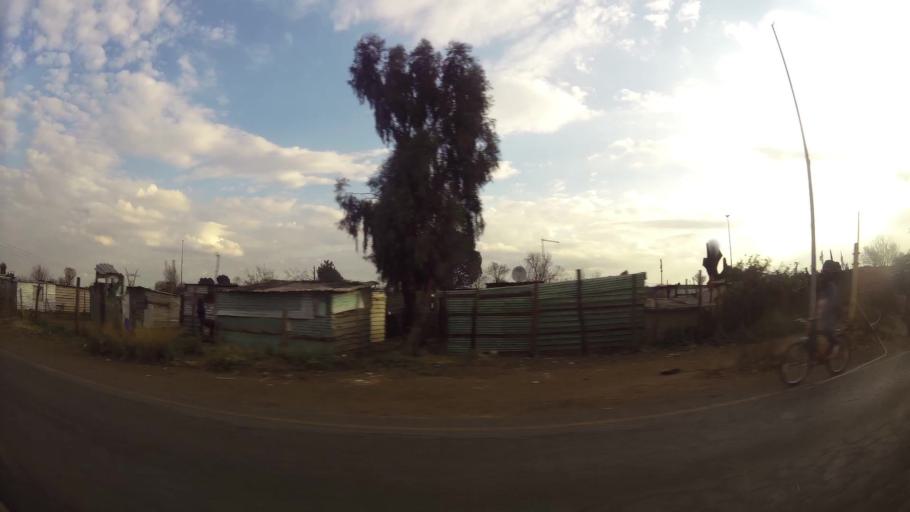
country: ZA
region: Gauteng
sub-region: Sedibeng District Municipality
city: Vanderbijlpark
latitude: -26.6916
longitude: 27.8041
